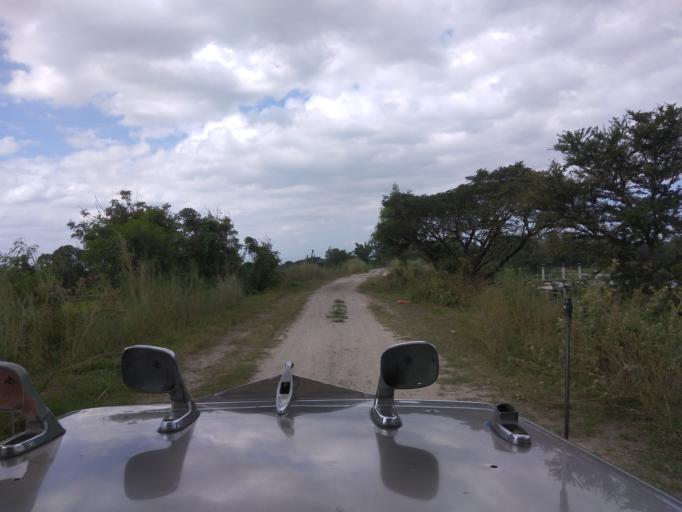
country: PH
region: Central Luzon
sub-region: Province of Pampanga
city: San Patricio
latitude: 15.1142
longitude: 120.7145
